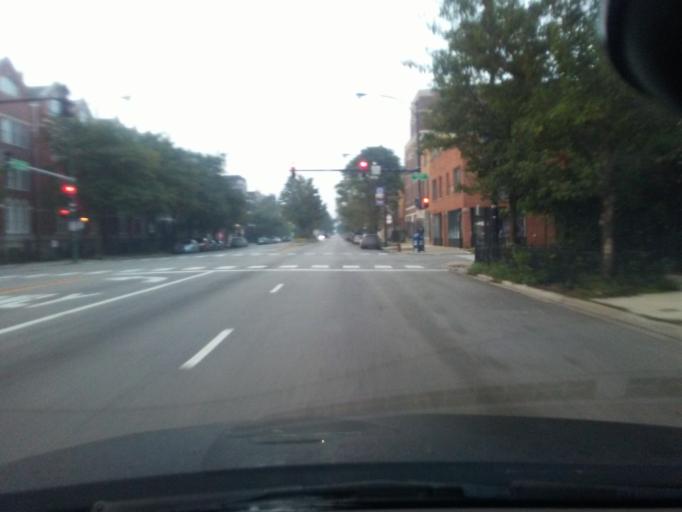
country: US
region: Illinois
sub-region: Cook County
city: Lincolnwood
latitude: 41.9509
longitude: -87.6690
